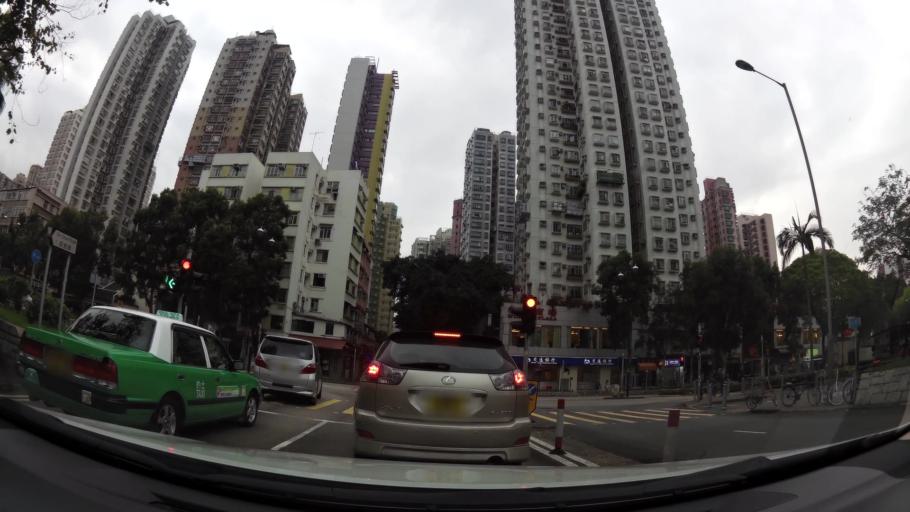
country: HK
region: Tai Po
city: Tai Po
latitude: 22.4529
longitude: 114.1660
